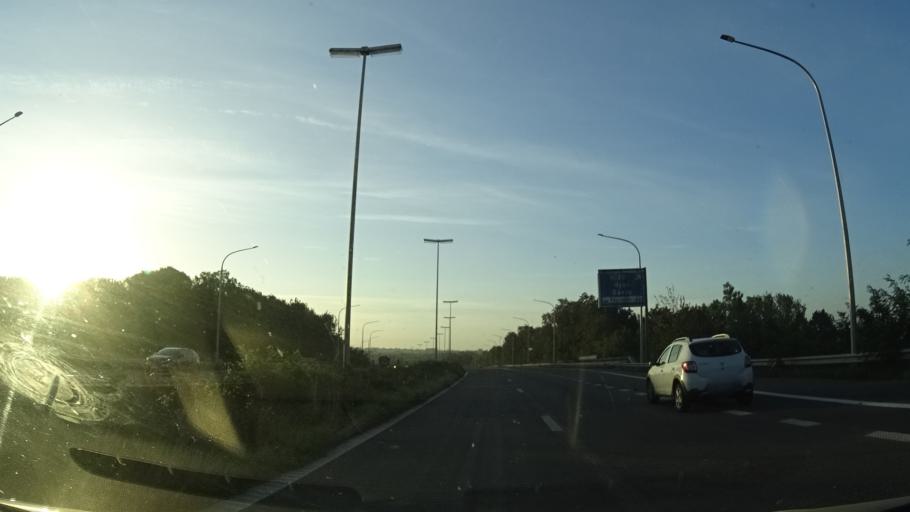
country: BE
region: Wallonia
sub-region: Province du Hainaut
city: Frameries
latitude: 50.4173
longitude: 3.9204
